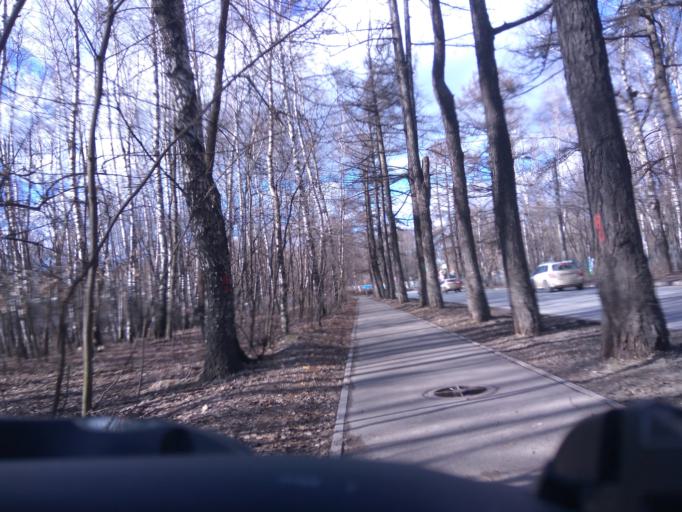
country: RU
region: Moscow
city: Sokol'niki
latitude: 55.7964
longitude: 37.6574
